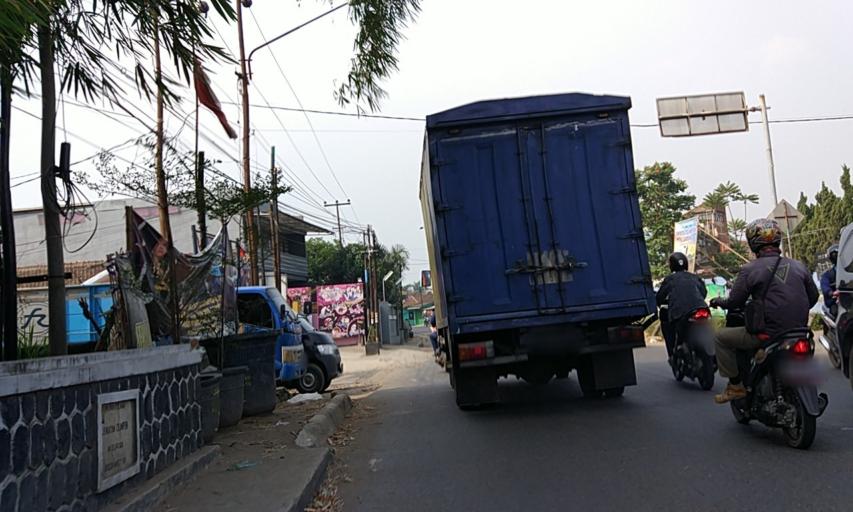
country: ID
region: West Java
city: Margahayukencana
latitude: -6.9848
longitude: 107.5628
